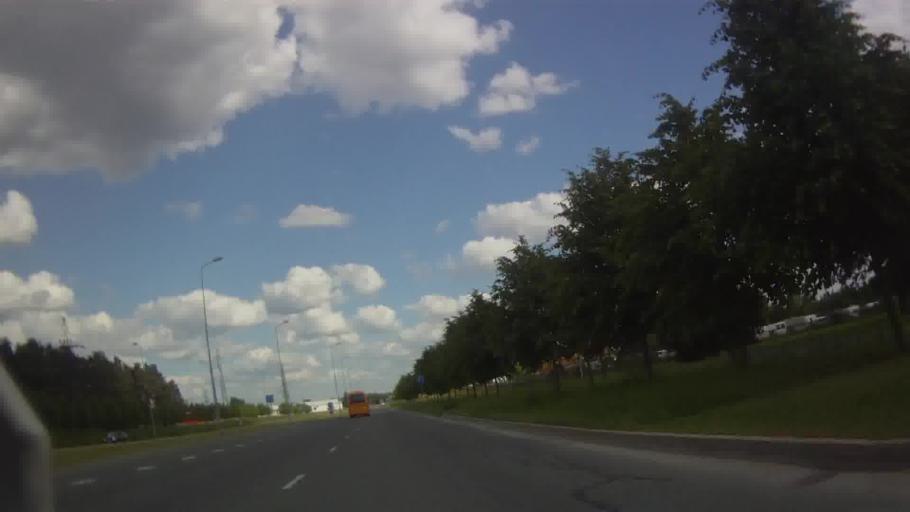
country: LV
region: Stopini
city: Ulbroka
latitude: 56.9535
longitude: 24.2117
